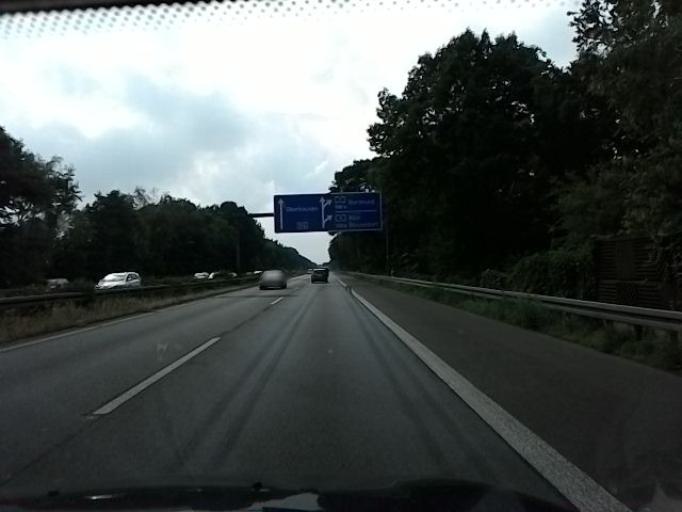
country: DE
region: North Rhine-Westphalia
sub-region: Regierungsbezirk Dusseldorf
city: Dinslaken
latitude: 51.5502
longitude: 6.8170
